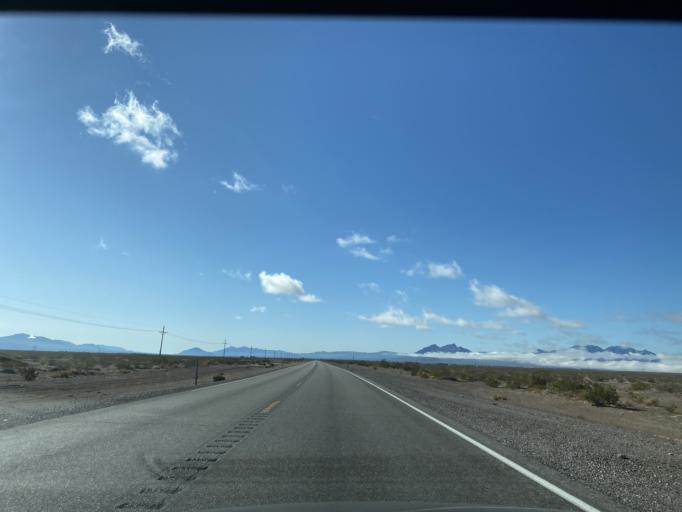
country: US
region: Nevada
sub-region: Nye County
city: Beatty
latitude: 36.5531
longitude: -116.4165
